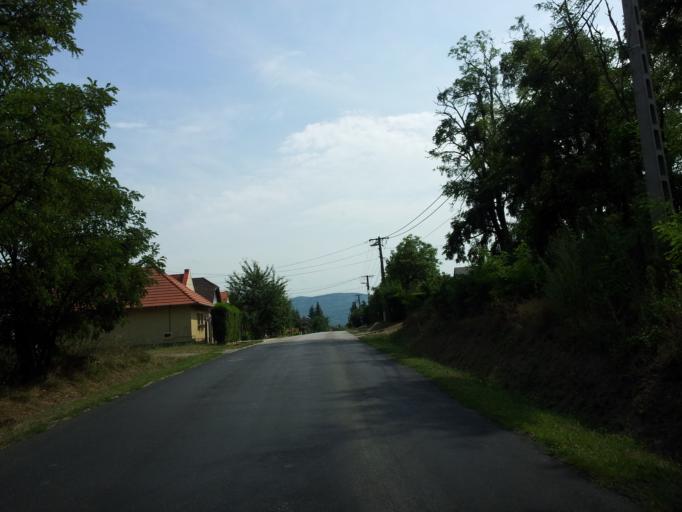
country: HU
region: Veszprem
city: Tapolca
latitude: 46.8480
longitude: 17.4645
